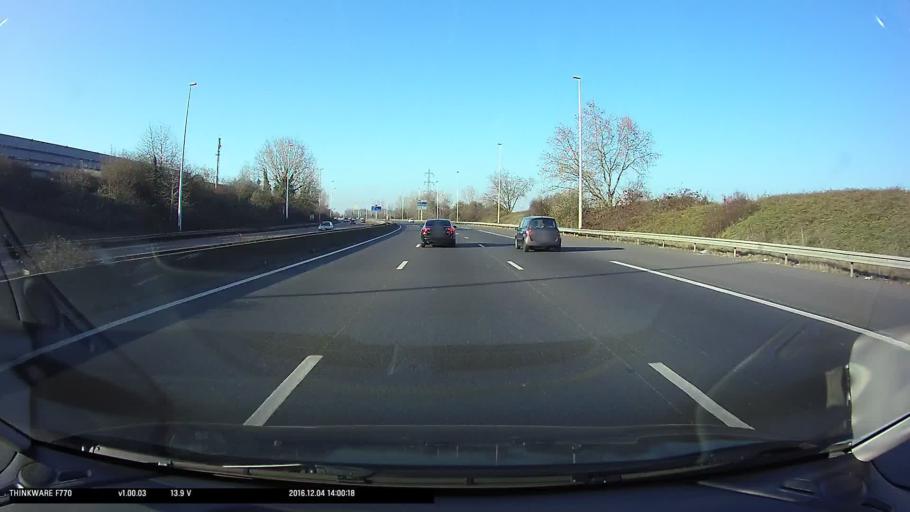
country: FR
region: Ile-de-France
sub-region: Departement du Val-d'Oise
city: Saint-Ouen-l'Aumone
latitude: 49.0285
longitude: 2.1282
